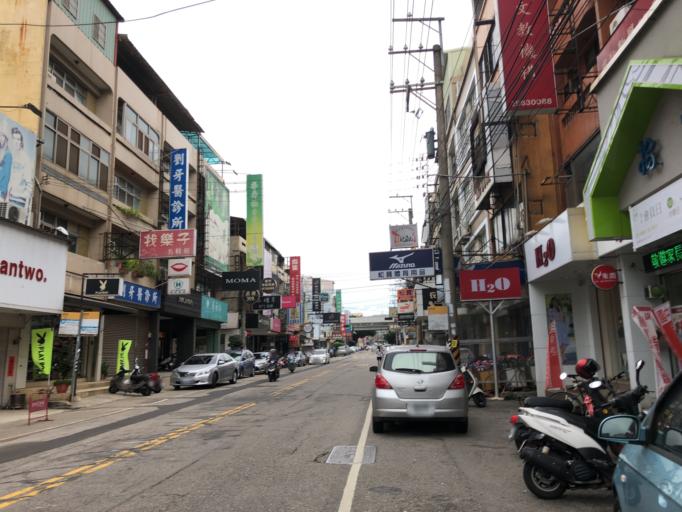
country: TW
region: Taiwan
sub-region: Taichung City
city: Taichung
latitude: 24.2377
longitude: 120.5620
